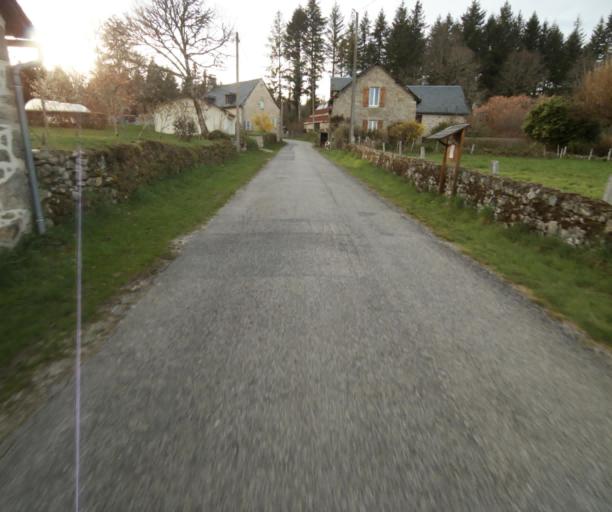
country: FR
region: Limousin
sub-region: Departement de la Correze
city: Argentat
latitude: 45.2206
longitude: 1.9691
